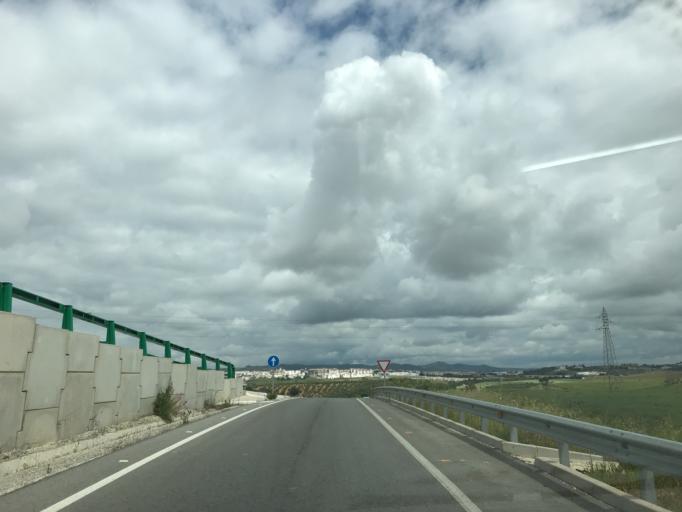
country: ES
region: Andalusia
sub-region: Provincia de Malaga
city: Ronda
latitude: 36.7269
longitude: -5.1469
